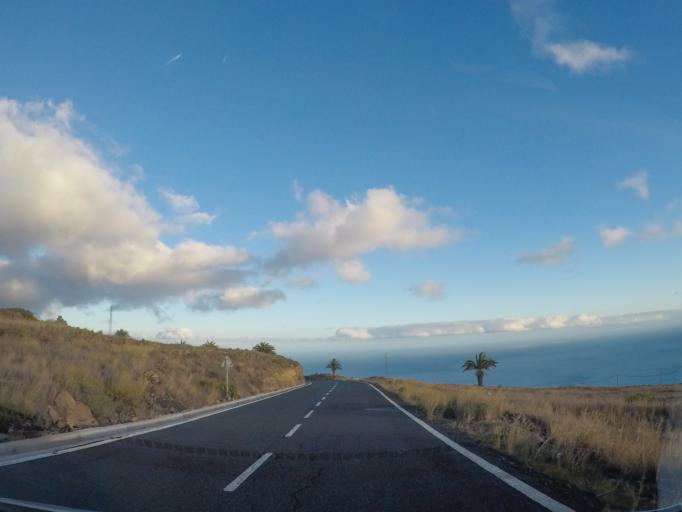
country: ES
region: Canary Islands
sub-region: Provincia de Santa Cruz de Tenerife
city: Alajero
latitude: 28.0484
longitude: -17.2319
